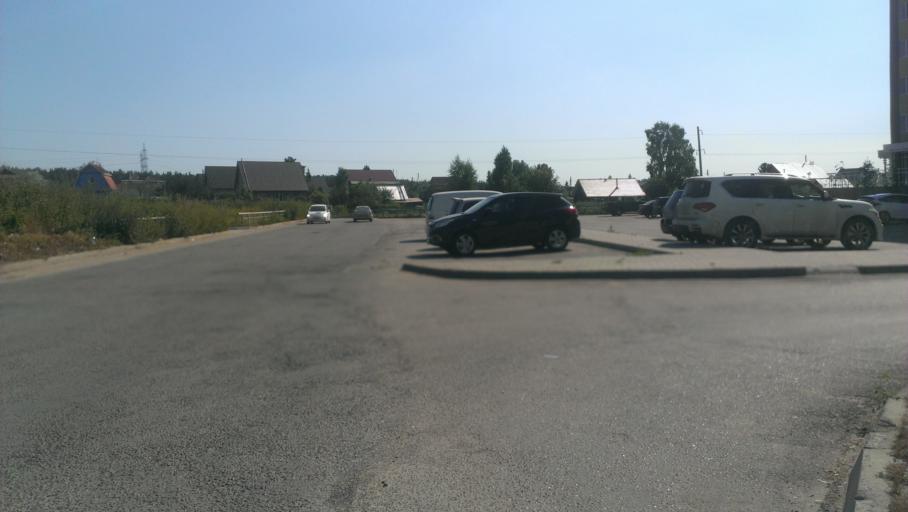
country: RU
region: Altai Krai
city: Novosilikatnyy
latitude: 53.3253
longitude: 83.6829
